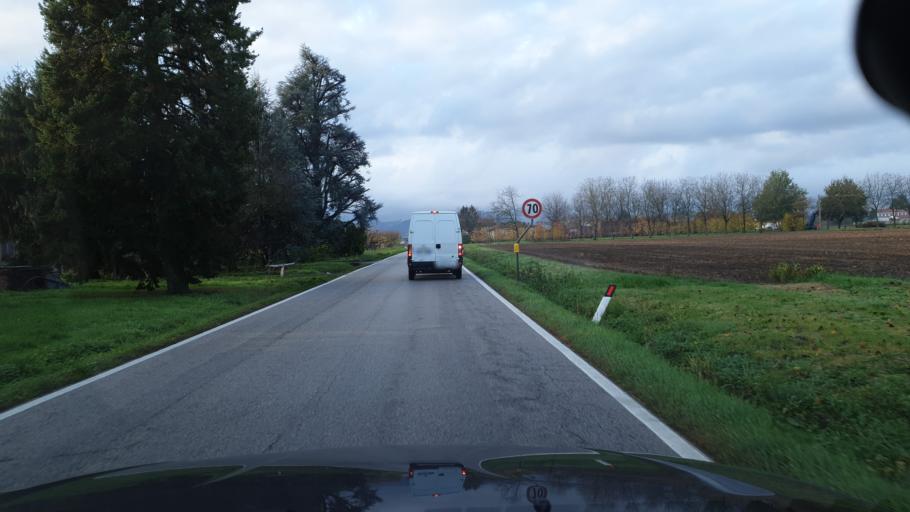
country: IT
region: Emilia-Romagna
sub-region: Provincia di Bologna
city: Crespellano
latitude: 44.5221
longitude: 11.1174
